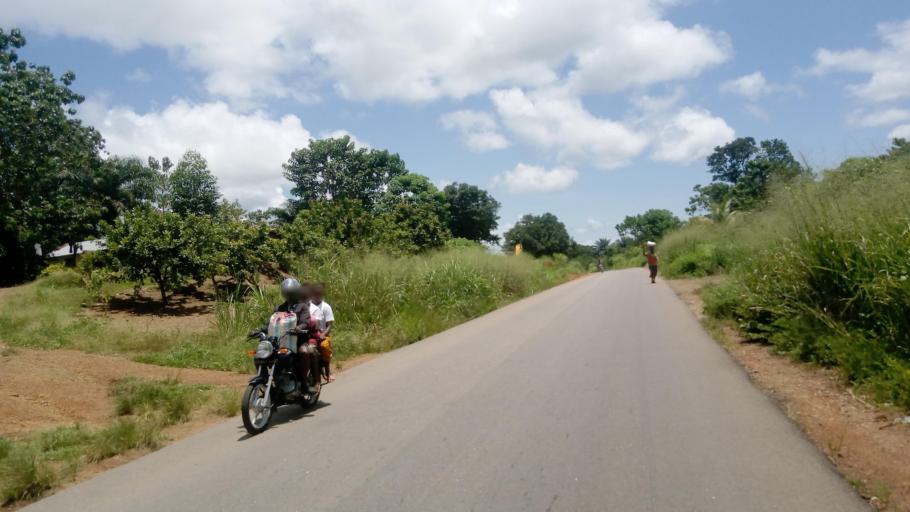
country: SL
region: Northern Province
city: Makeni
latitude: 8.9226
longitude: -12.0203
